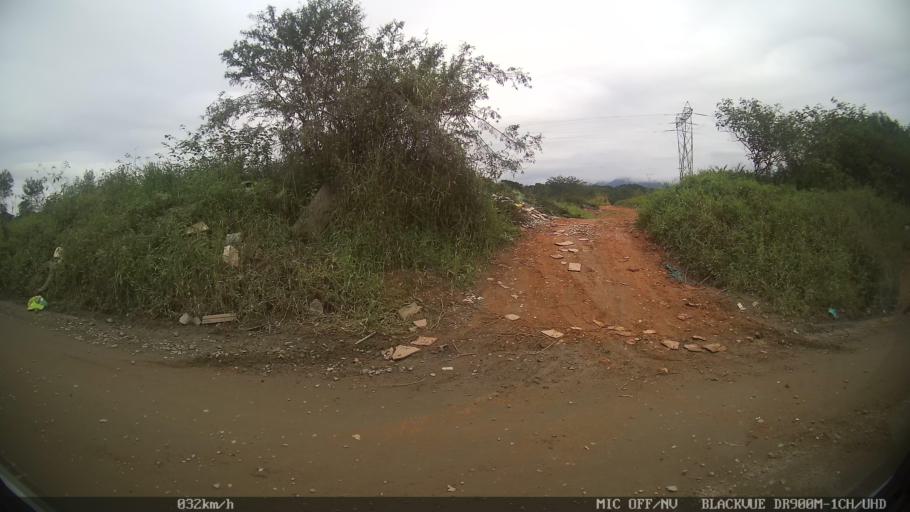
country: BR
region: Santa Catarina
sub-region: Joinville
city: Joinville
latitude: -26.2754
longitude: -48.8910
